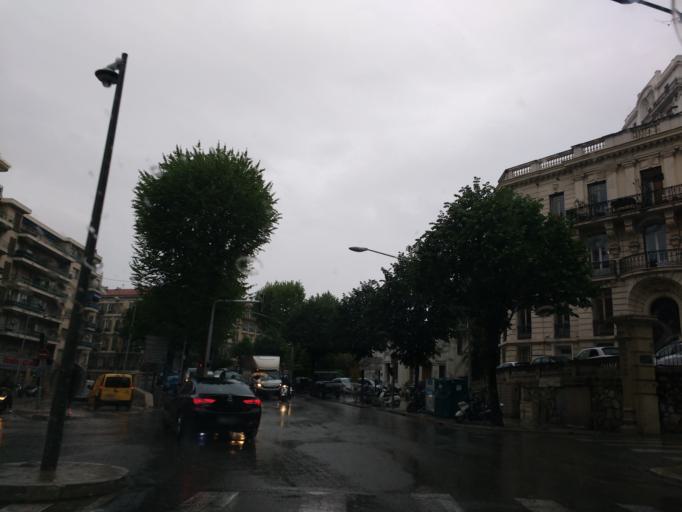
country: FR
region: Provence-Alpes-Cote d'Azur
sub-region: Departement des Alpes-Maritimes
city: Nice
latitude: 43.7053
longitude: 7.2720
